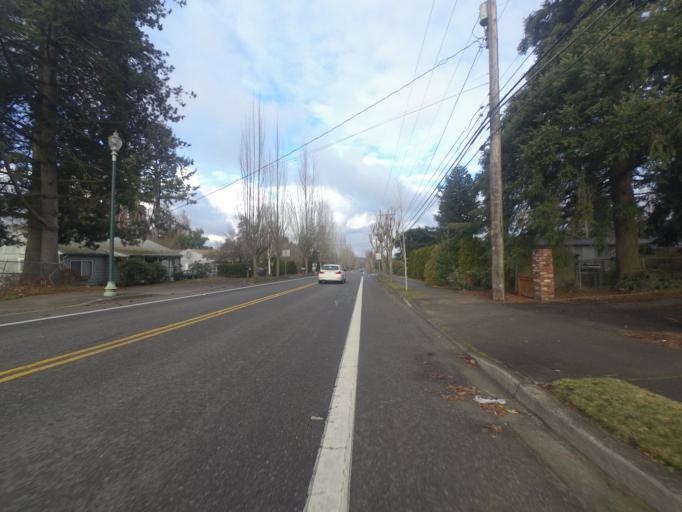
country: US
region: Washington
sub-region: Pierce County
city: University Place
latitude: 47.2284
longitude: -122.5504
